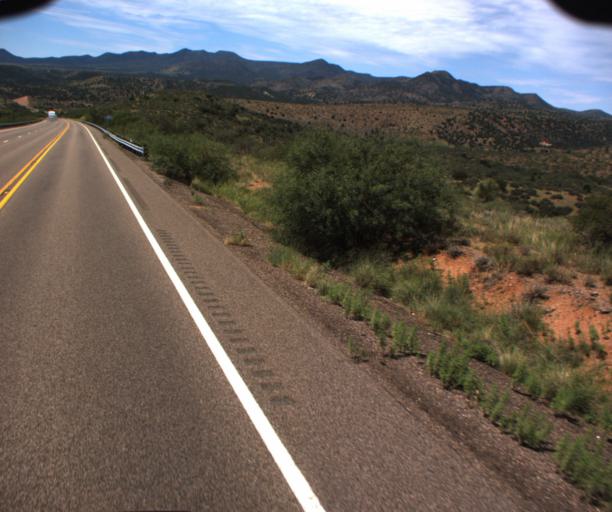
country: US
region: Arizona
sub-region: Gila County
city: Globe
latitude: 33.5969
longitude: -110.6383
